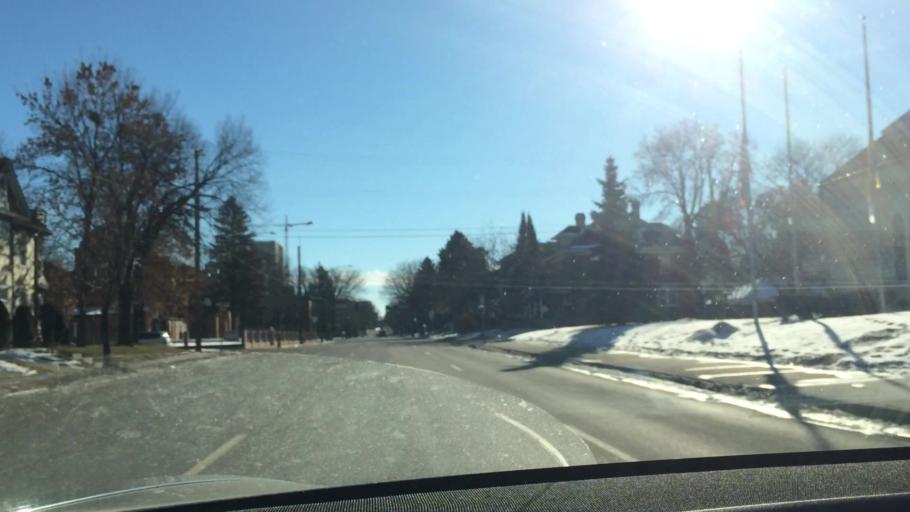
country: US
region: Minnesota
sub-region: Hennepin County
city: Minneapolis
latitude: 44.9948
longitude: -93.2611
